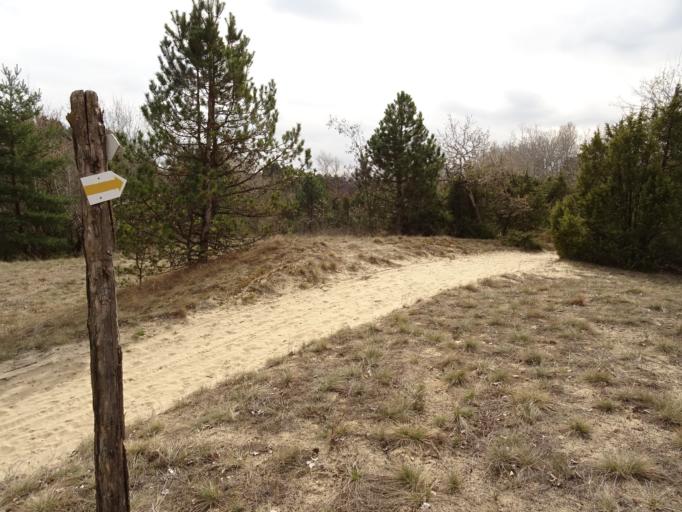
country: HU
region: Bacs-Kiskun
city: Izsak
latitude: 46.8313
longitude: 19.3024
